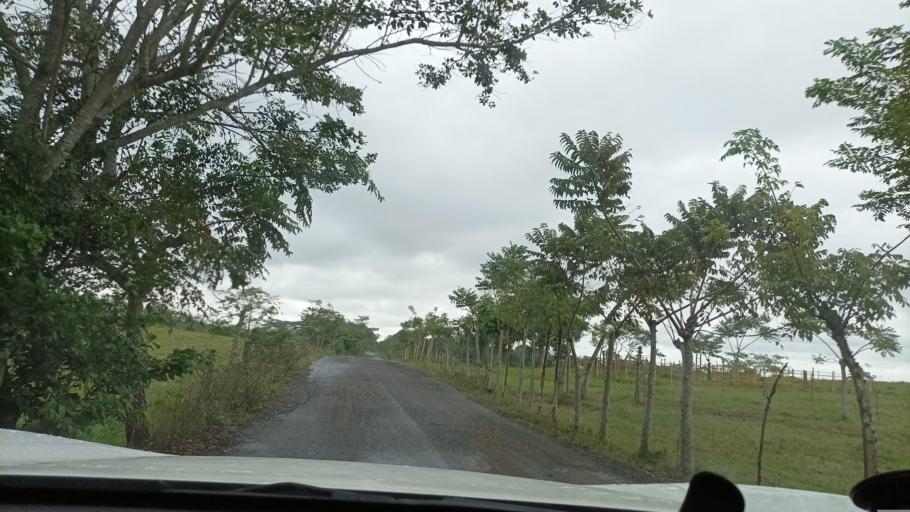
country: MX
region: Veracruz
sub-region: Moloacan
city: Cuichapa
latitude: 17.7686
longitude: -94.3886
